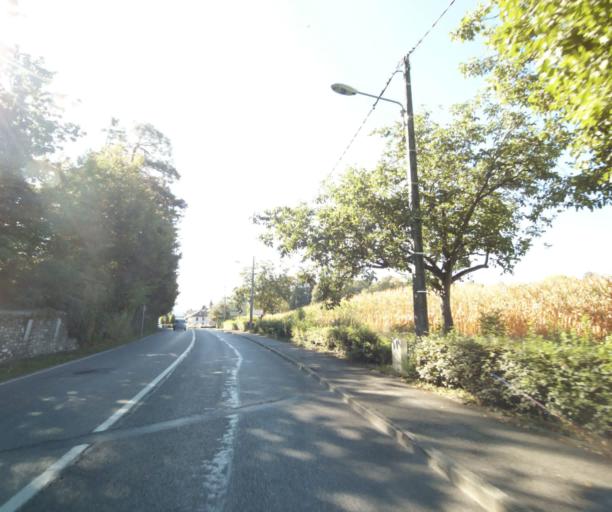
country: FR
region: Rhone-Alpes
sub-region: Departement de l'Ain
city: Ferney-Voltaire
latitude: 46.2607
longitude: 6.1047
